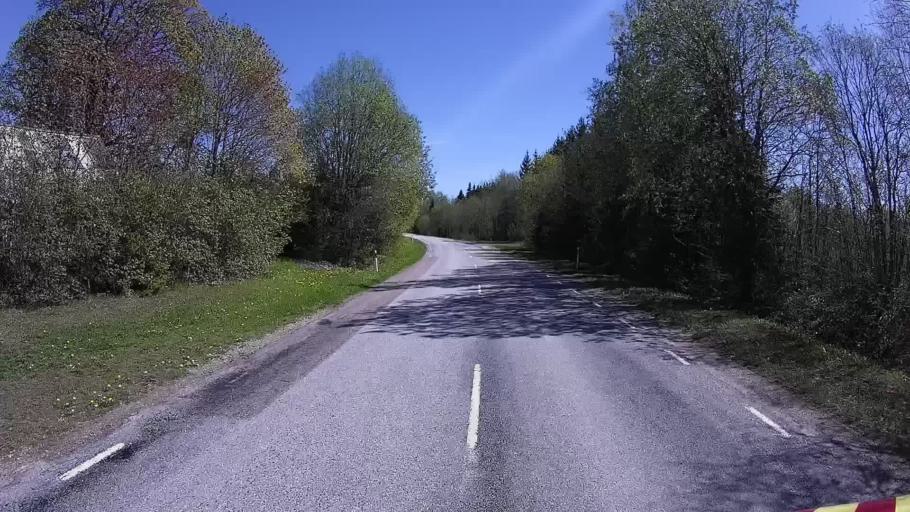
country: EE
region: Raplamaa
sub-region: Kehtna vald
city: Kehtna
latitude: 59.0385
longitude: 25.0415
